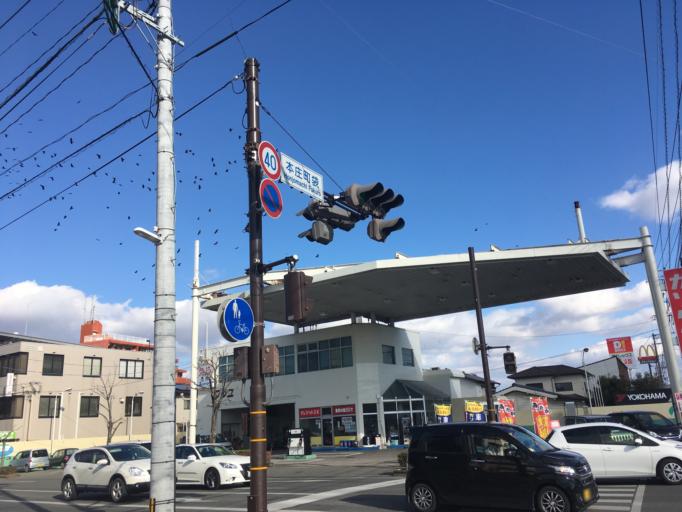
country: JP
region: Saga Prefecture
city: Saga-shi
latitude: 33.2390
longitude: 130.3019
